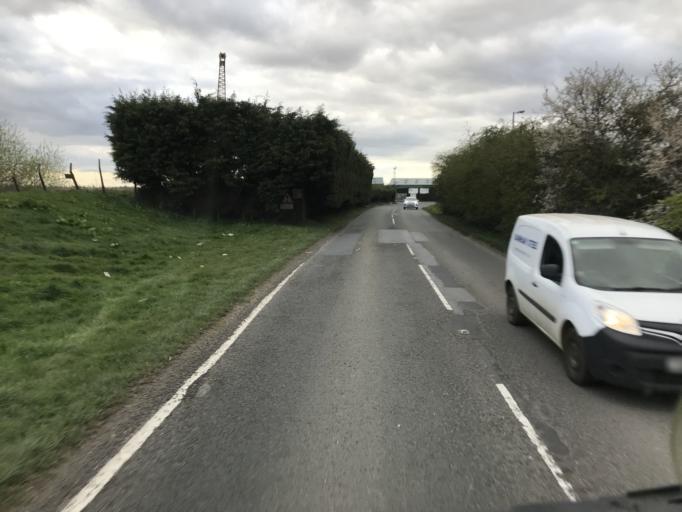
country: GB
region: England
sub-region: North Lincolnshire
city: Burton upon Stather
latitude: 53.6172
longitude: -0.6990
